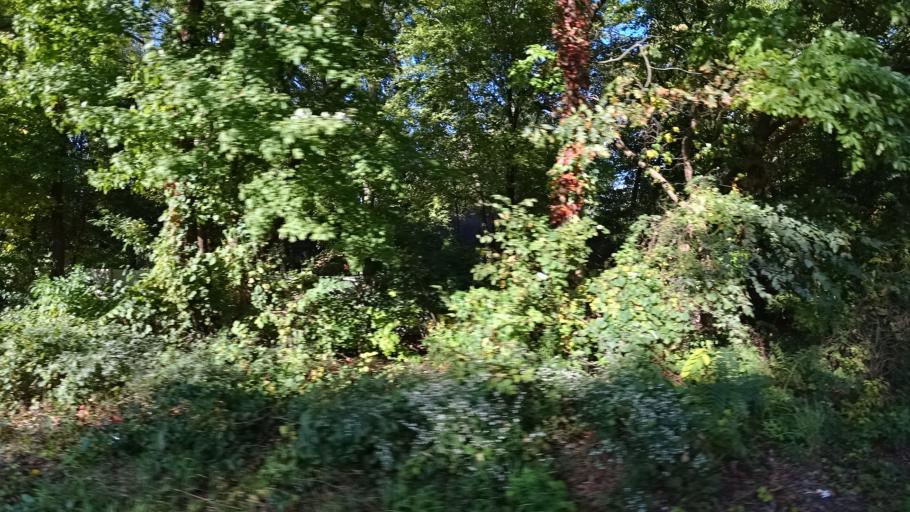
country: US
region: Indiana
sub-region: LaPorte County
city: Trail Creek
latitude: 41.6962
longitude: -86.8745
